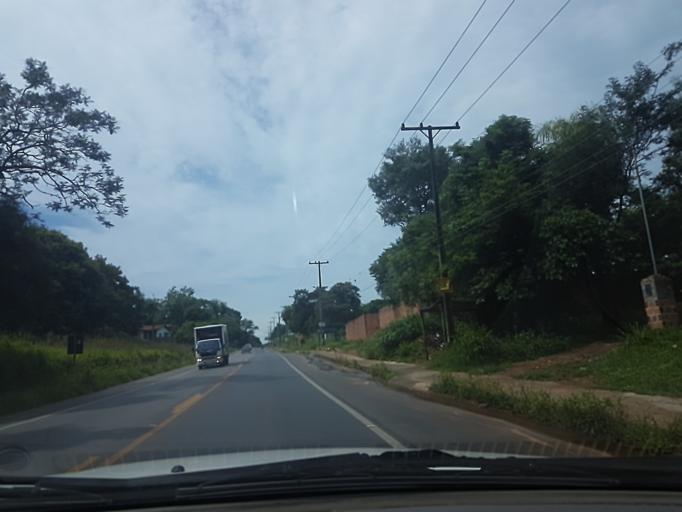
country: PY
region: Central
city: Limpio
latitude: -25.2459
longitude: -57.4580
